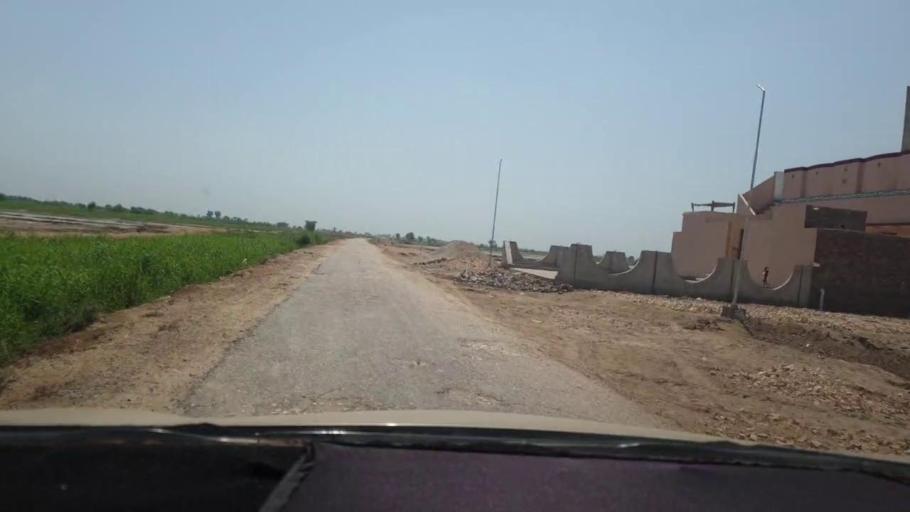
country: PK
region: Sindh
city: Shahdadkot
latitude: 27.8459
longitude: 67.9482
